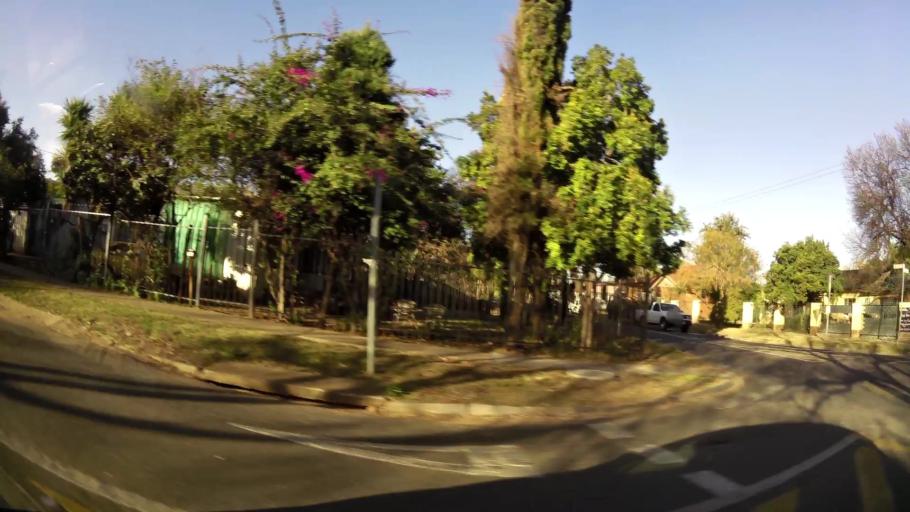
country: ZA
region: Gauteng
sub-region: City of Tshwane Metropolitan Municipality
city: Pretoria
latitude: -25.7024
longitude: 28.2046
